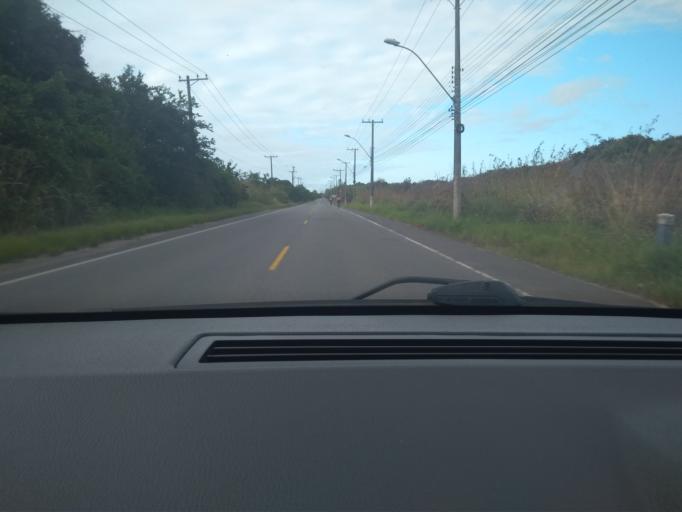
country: BR
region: Espirito Santo
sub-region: Serra
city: Serra
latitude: -20.0970
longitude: -40.1761
